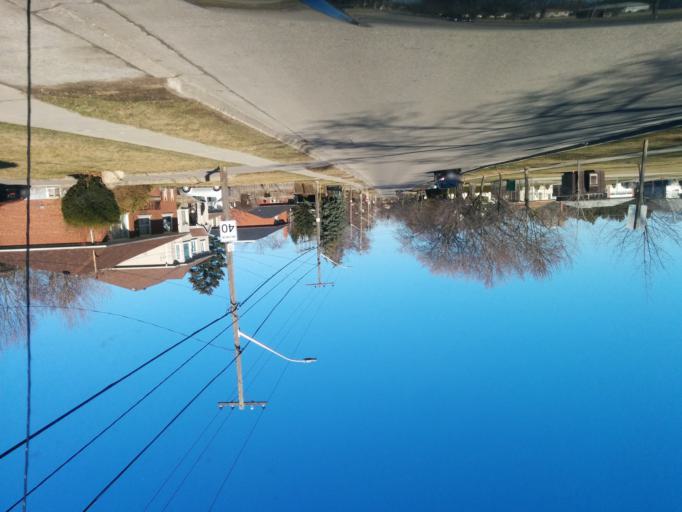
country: CA
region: Ontario
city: Etobicoke
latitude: 43.5808
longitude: -79.5665
